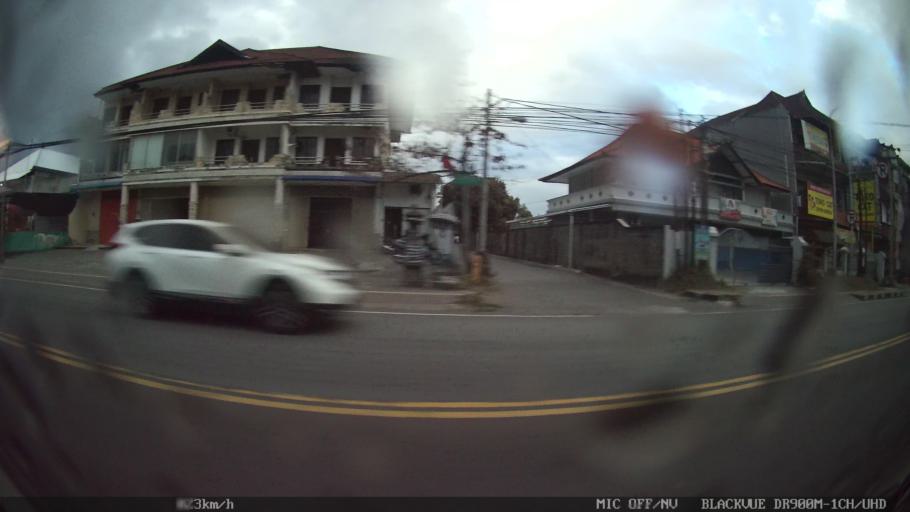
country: ID
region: Bali
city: Banjar Kayangan
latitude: -8.6355
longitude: 115.2309
